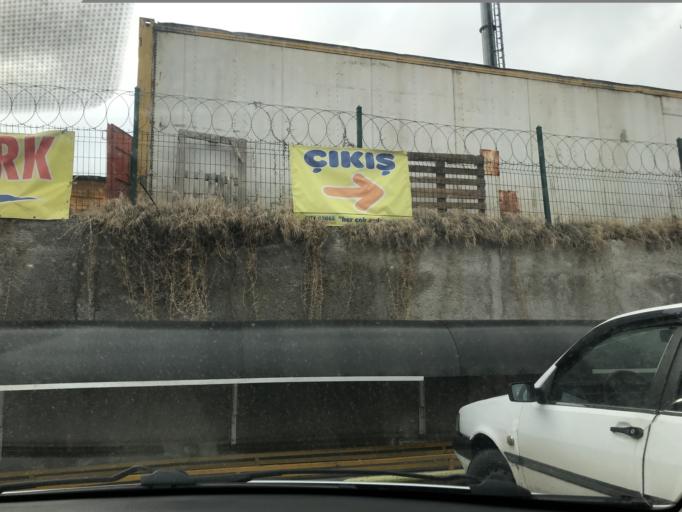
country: TR
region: Ankara
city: Batikent
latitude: 39.9647
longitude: 32.7544
